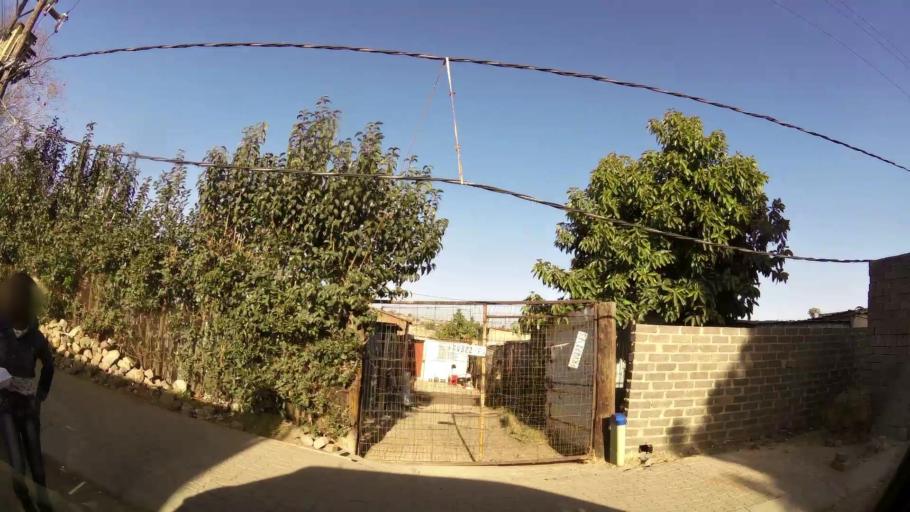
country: ZA
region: Gauteng
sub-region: City of Johannesburg Metropolitan Municipality
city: Diepsloot
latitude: -25.9305
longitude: 28.0074
